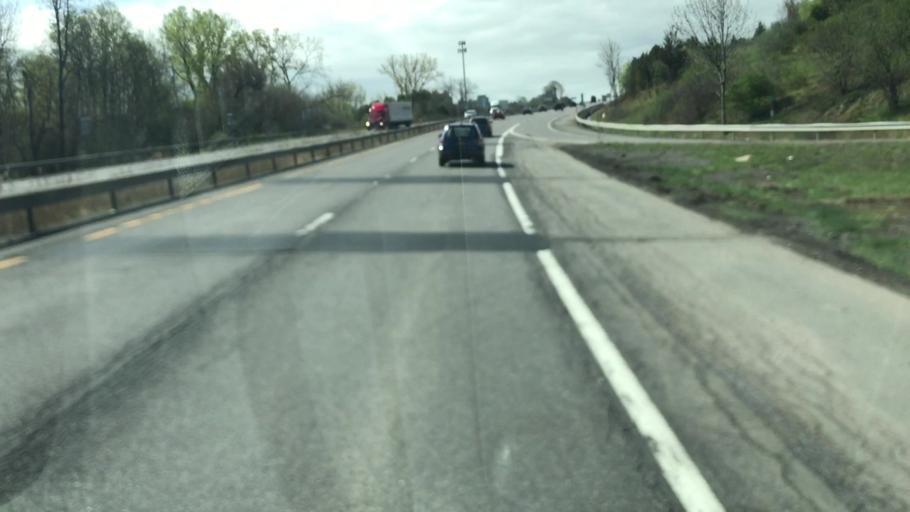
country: US
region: New York
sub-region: Onondaga County
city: Nedrow
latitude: 42.8910
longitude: -76.1097
